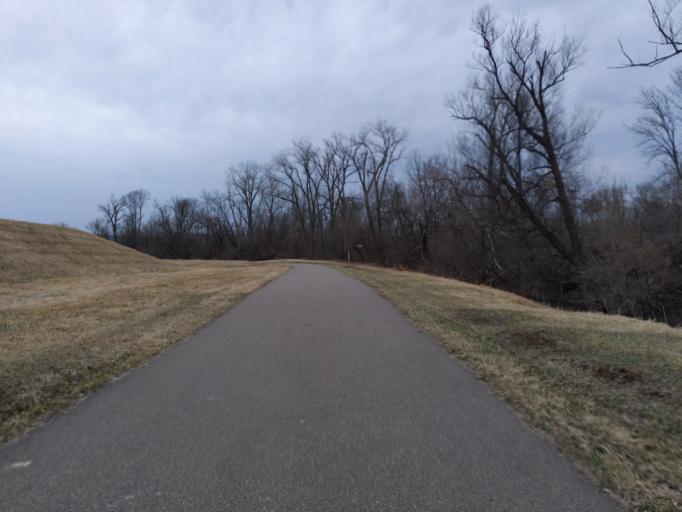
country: US
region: New York
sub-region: Chemung County
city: Elmira
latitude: 42.0969
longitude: -76.7899
